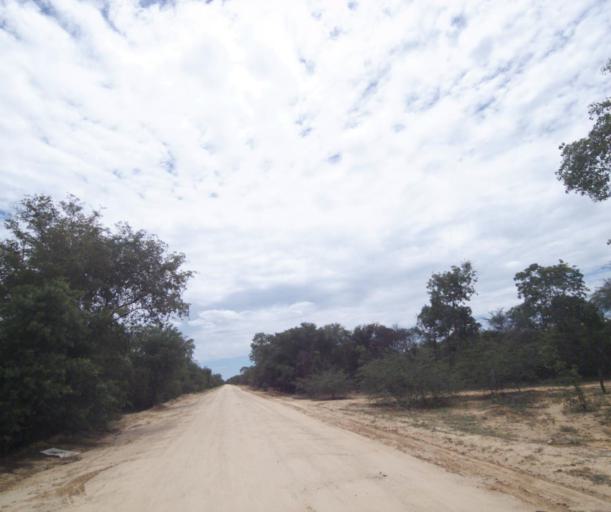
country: BR
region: Bahia
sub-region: Carinhanha
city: Carinhanha
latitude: -14.2116
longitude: -43.9274
